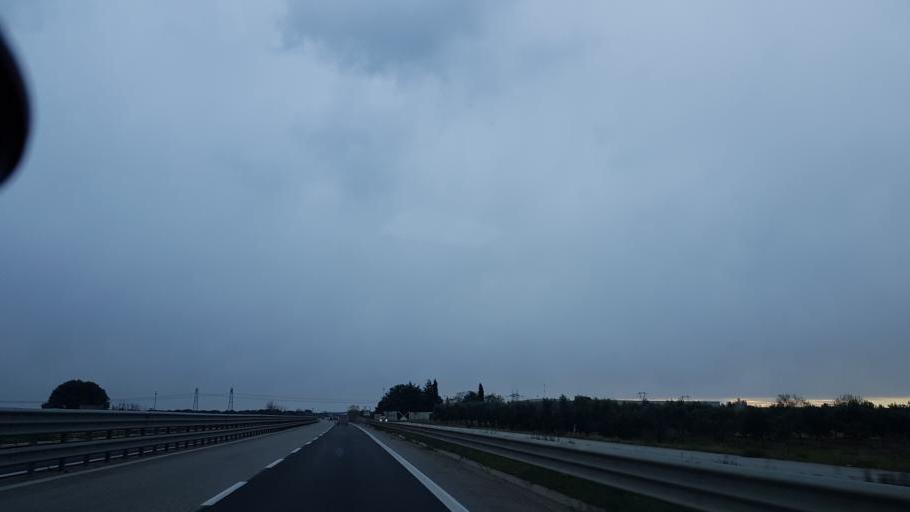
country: IT
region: Apulia
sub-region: Provincia di Brindisi
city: Mesagne
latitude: 40.5829
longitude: 17.8457
